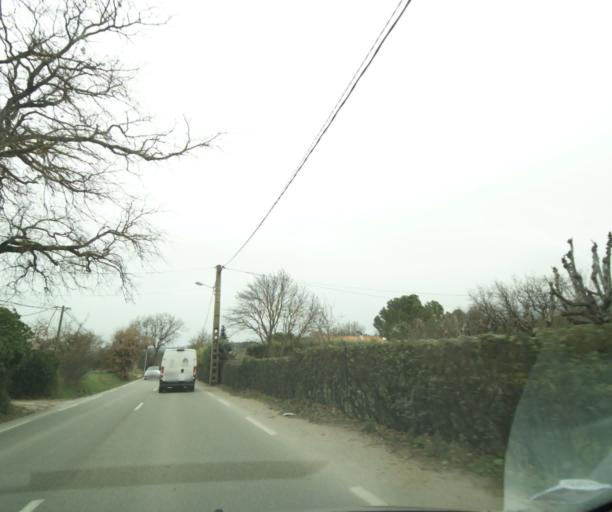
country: FR
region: Provence-Alpes-Cote d'Azur
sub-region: Departement des Bouches-du-Rhone
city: Fuveau
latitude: 43.4716
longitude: 5.5448
